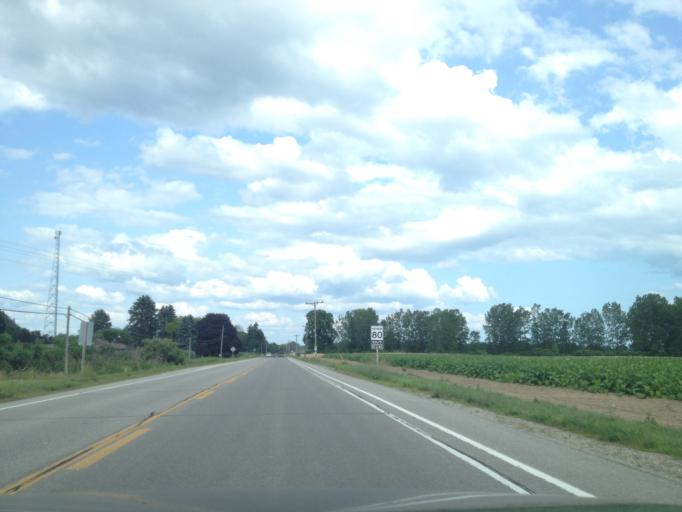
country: CA
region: Ontario
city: Aylmer
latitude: 42.6624
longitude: -81.0048
